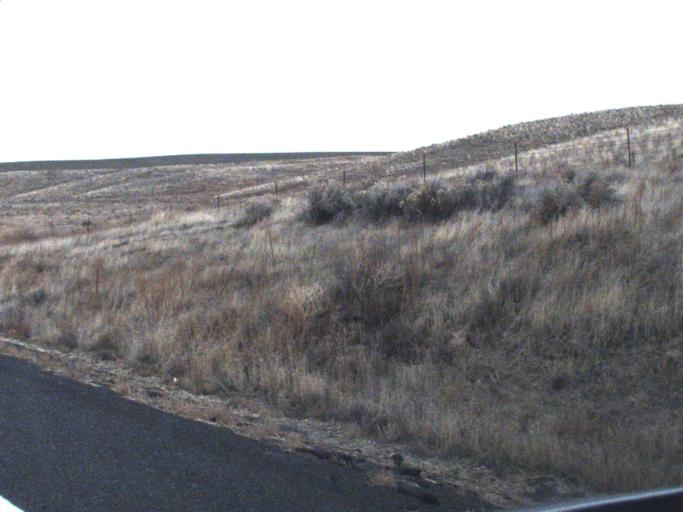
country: US
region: Washington
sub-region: Garfield County
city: Pomeroy
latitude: 46.7848
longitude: -117.9265
